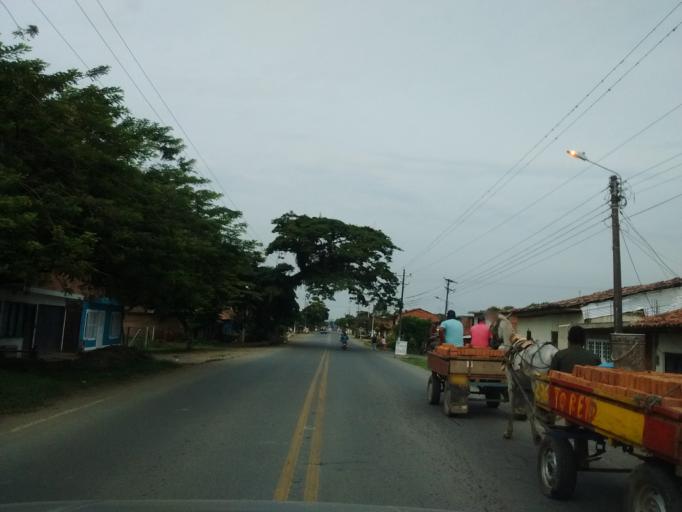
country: CO
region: Cauca
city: Puerto Tejada
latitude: 3.1800
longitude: -76.4537
